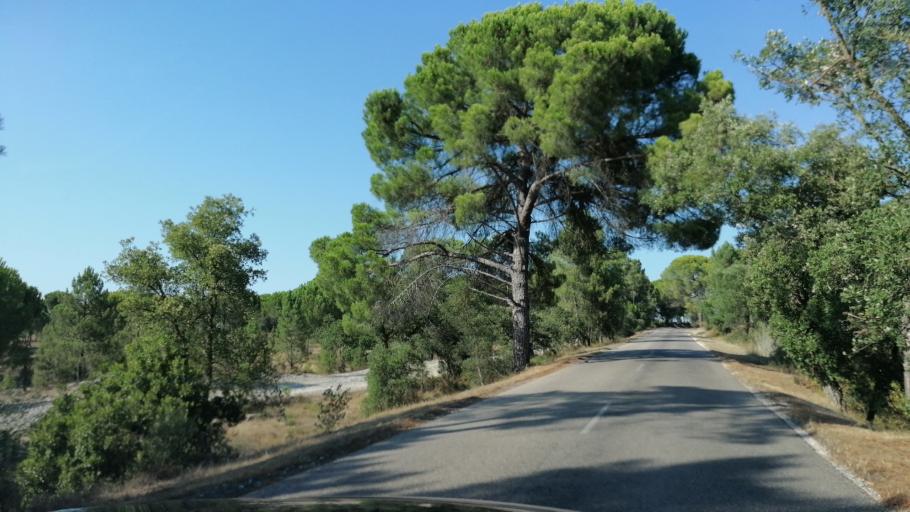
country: PT
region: Santarem
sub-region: Coruche
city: Coruche
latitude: 38.8987
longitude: -8.5323
